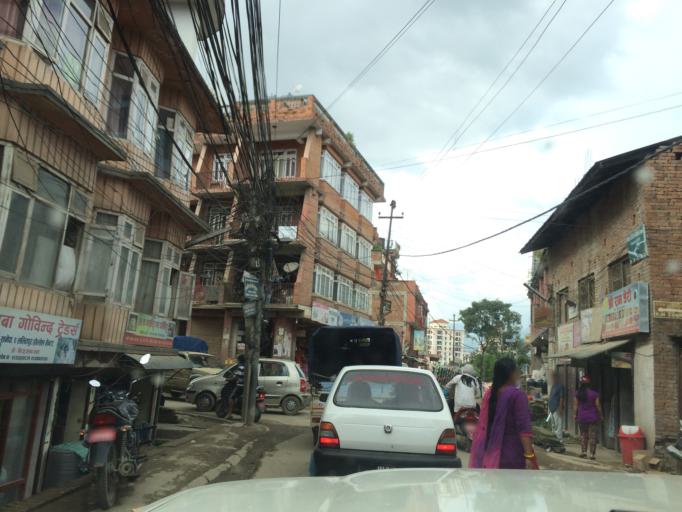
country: NP
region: Central Region
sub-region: Bagmati Zone
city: Patan
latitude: 27.6909
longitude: 85.3055
